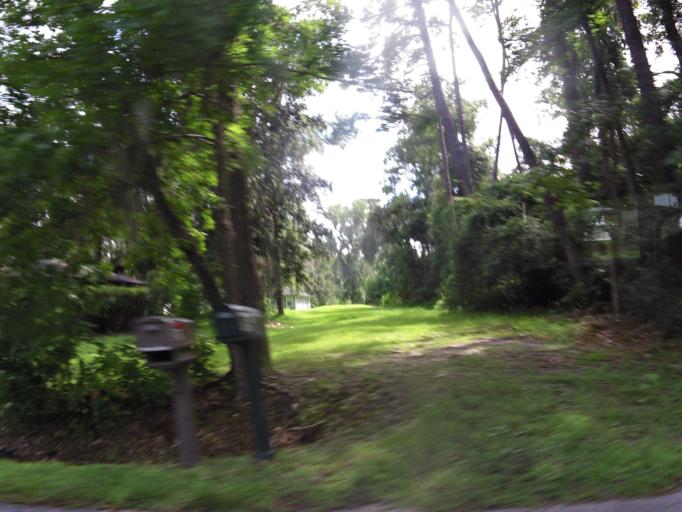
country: US
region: Florida
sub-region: Clay County
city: Lakeside
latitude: 30.1237
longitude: -81.7623
